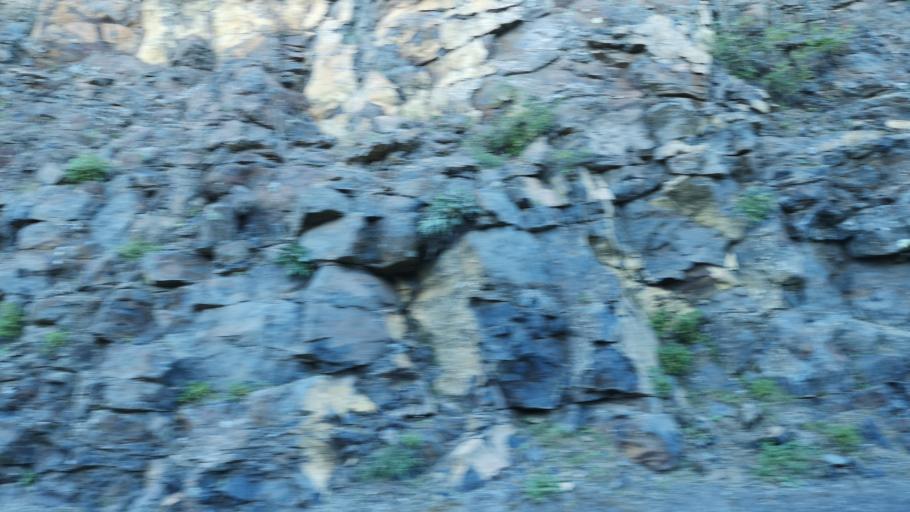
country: ES
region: Canary Islands
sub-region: Provincia de Santa Cruz de Tenerife
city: Alajero
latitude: 28.0912
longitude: -17.2482
